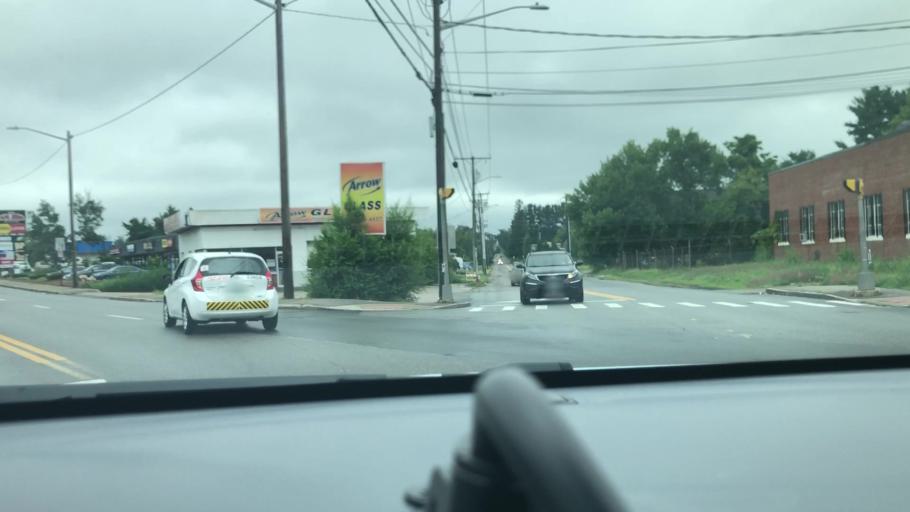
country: US
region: New Hampshire
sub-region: Hillsborough County
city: Manchester
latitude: 42.9713
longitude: -71.4553
